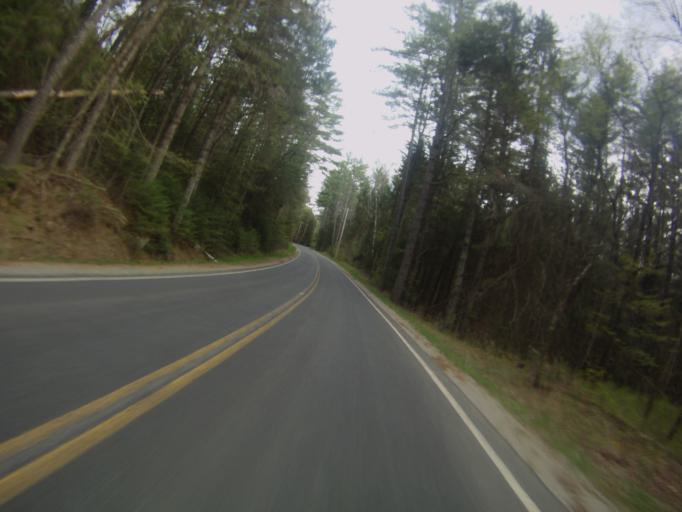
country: US
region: New York
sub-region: Warren County
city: Warrensburg
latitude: 43.8080
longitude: -73.9387
